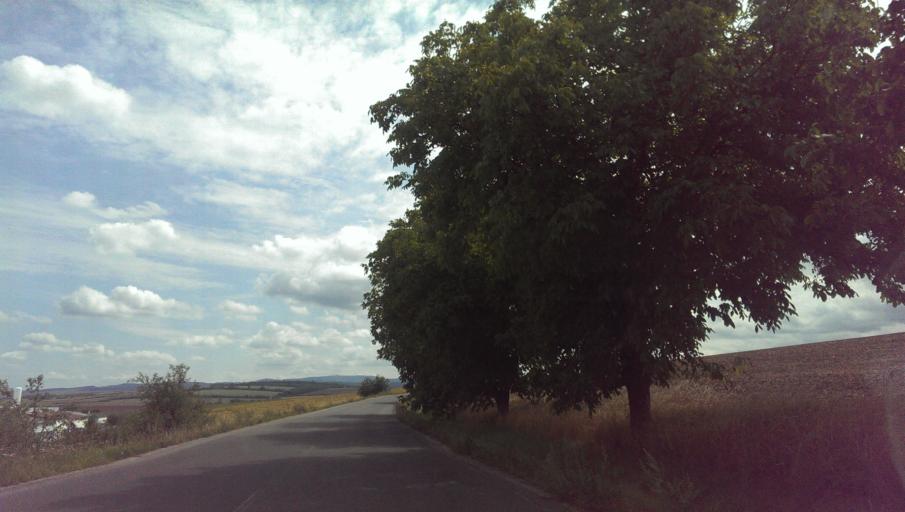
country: CZ
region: Zlin
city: Hluk
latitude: 48.9805
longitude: 17.5344
